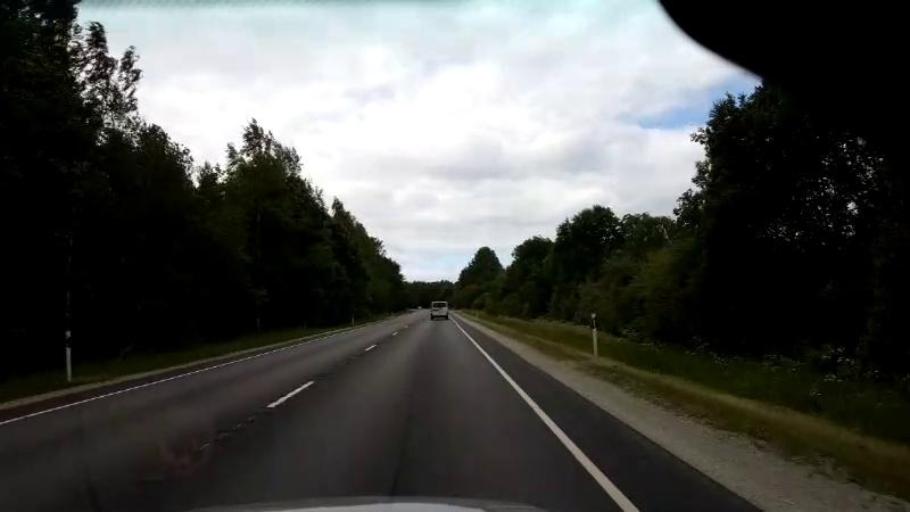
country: EE
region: Paernumaa
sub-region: Paernu linn
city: Parnu
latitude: 58.2250
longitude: 24.4926
